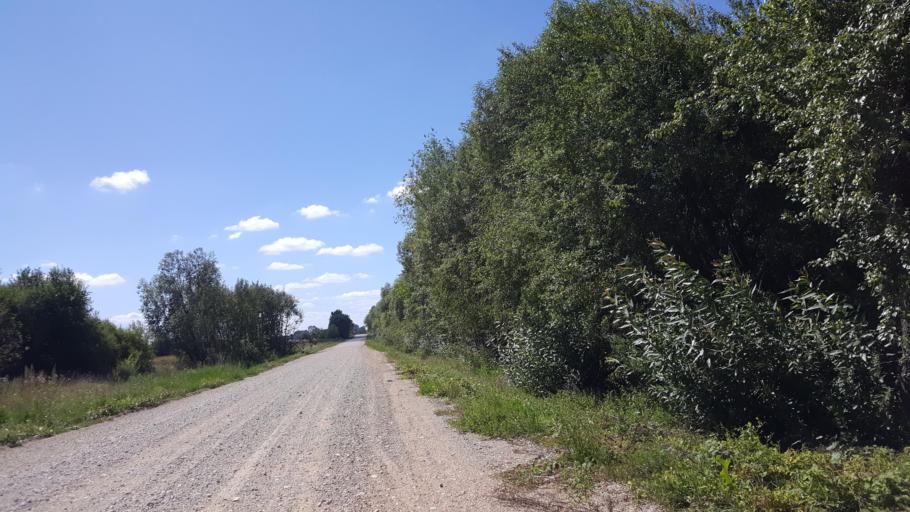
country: BY
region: Brest
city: Horad Kobryn
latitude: 52.3126
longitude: 24.3892
